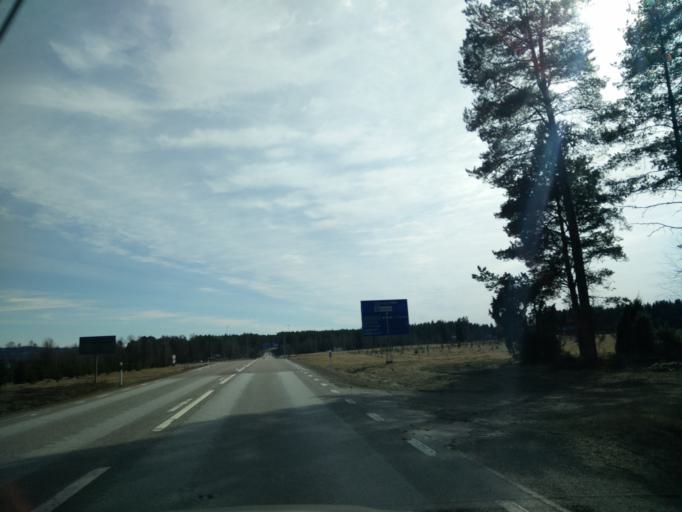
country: SE
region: Vaermland
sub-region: Hagfors Kommun
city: Hagfors
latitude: 60.0379
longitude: 13.5867
